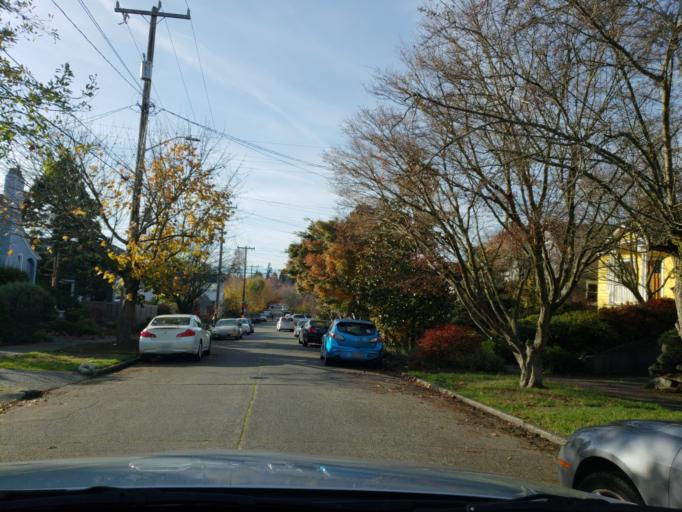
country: US
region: Washington
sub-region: King County
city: Shoreline
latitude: 47.6818
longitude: -122.3596
